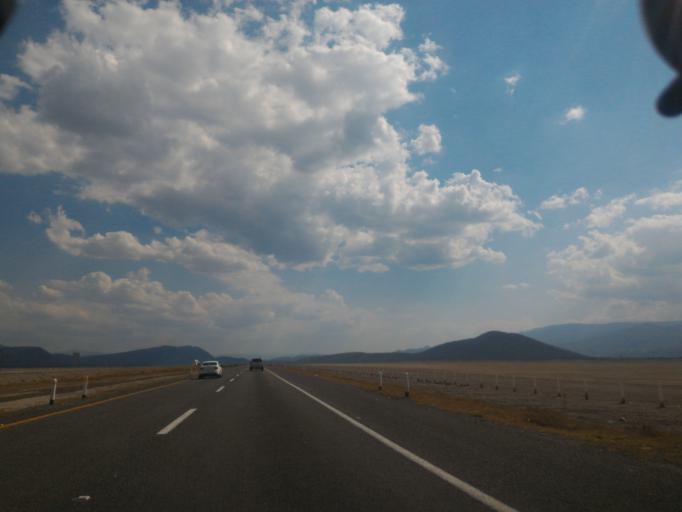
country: MX
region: Jalisco
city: Zacoalco de Torres
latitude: 20.3027
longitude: -103.5596
